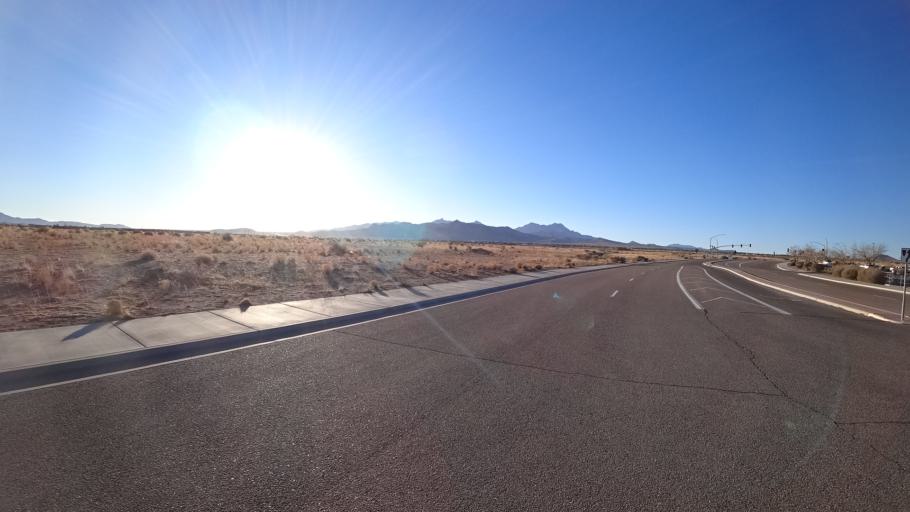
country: US
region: Arizona
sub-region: Mohave County
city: New Kingman-Butler
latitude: 35.2199
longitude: -113.9837
